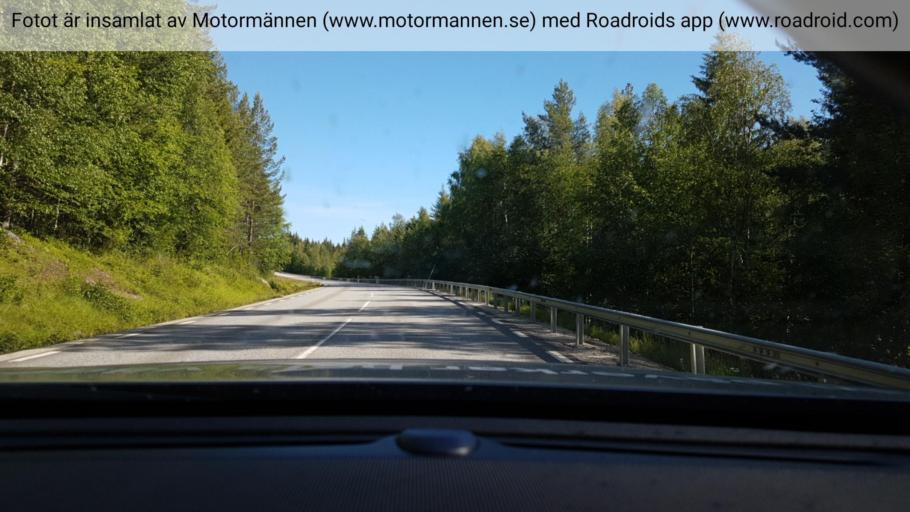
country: SE
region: Vaesterbotten
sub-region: Lycksele Kommun
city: Lycksele
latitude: 64.6533
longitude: 18.4581
